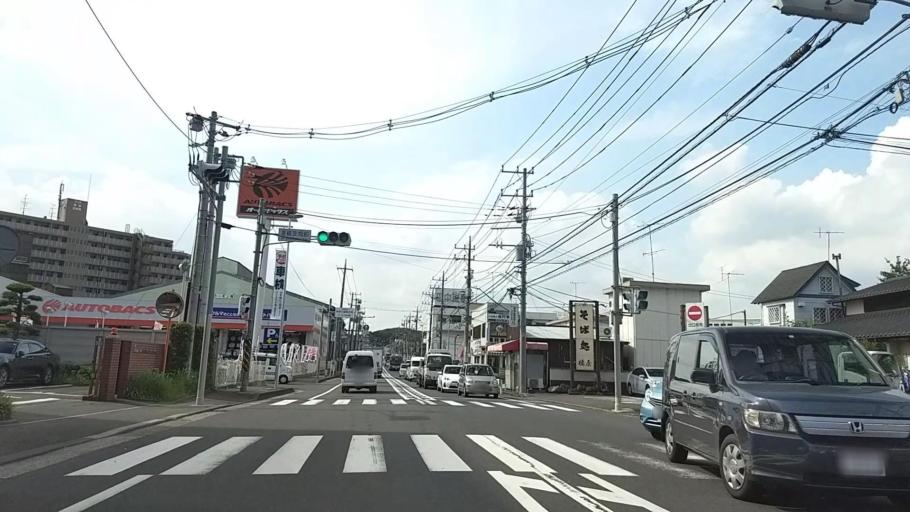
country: JP
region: Kanagawa
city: Yokohama
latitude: 35.5185
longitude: 139.5740
